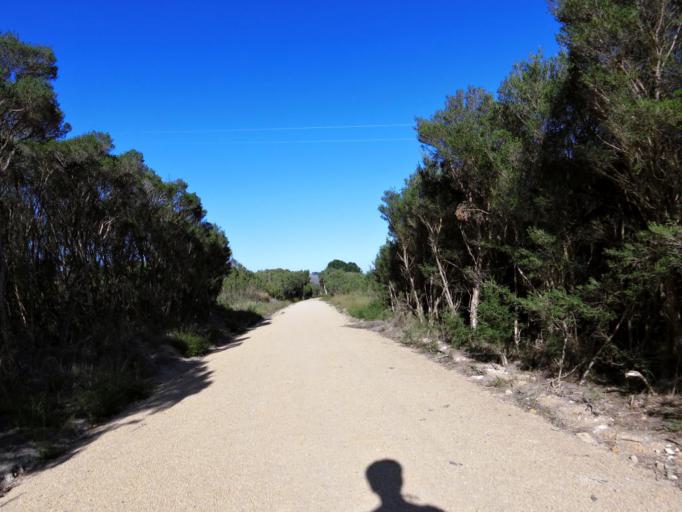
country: AU
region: Victoria
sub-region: Bass Coast
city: North Wonthaggi
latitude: -38.5013
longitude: 145.5012
